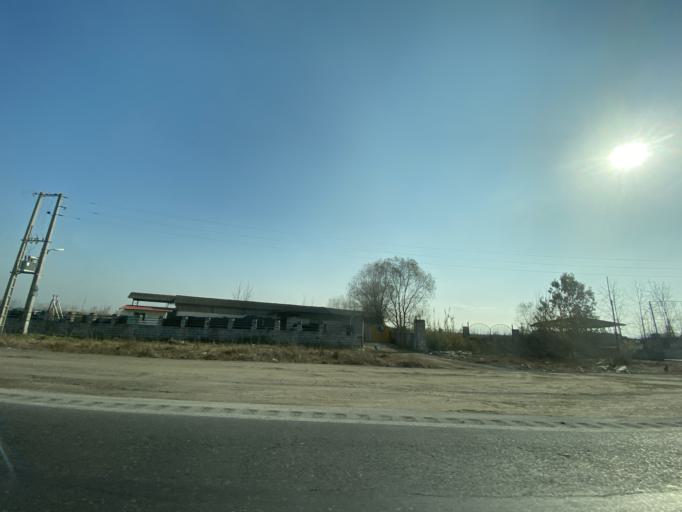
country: IR
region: Mazandaran
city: Amol
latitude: 36.4897
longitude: 52.4941
